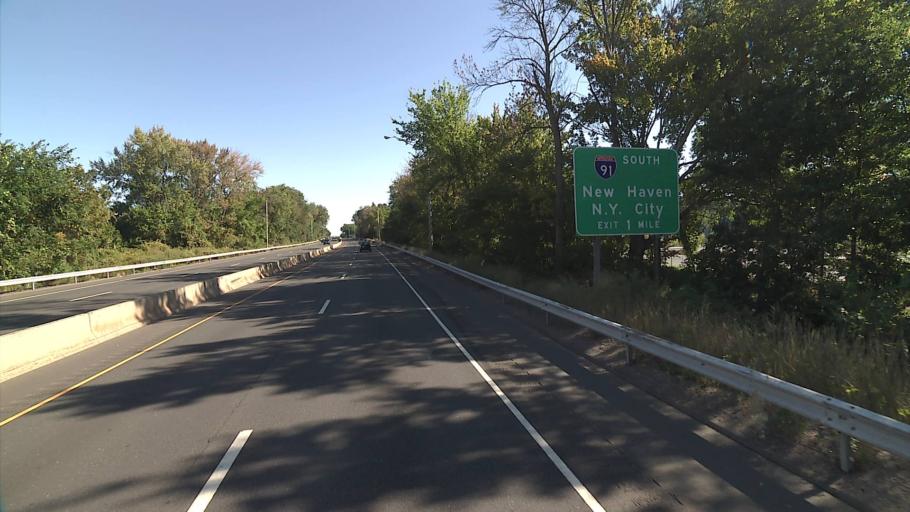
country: US
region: Connecticut
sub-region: Hartford County
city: Wethersfield
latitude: 41.7205
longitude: -72.6771
